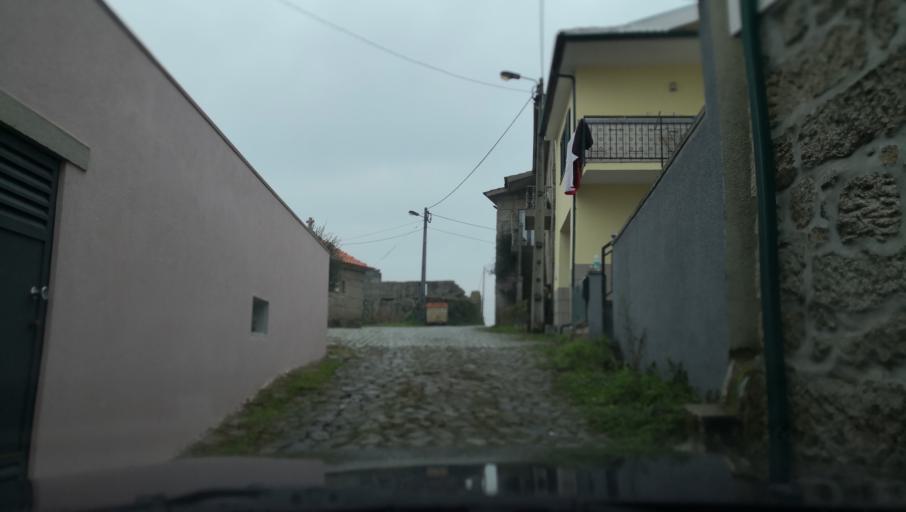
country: PT
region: Vila Real
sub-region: Vila Real
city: Vila Real
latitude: 41.2987
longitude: -7.7797
